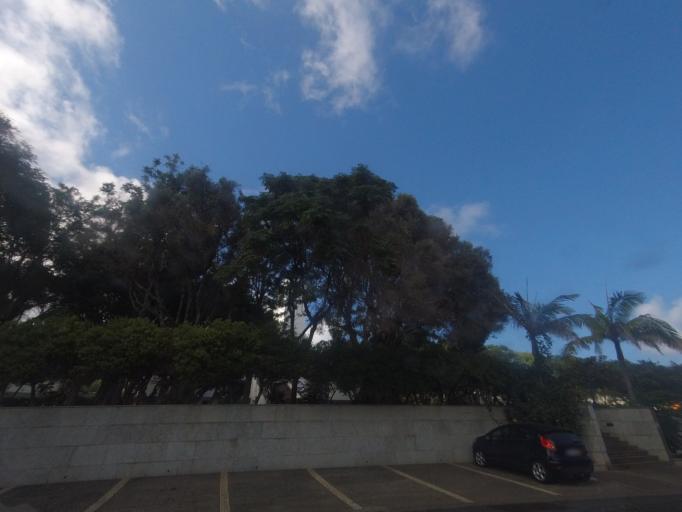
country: PT
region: Madeira
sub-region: Machico
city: Canical
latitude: 32.7384
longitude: -16.7364
